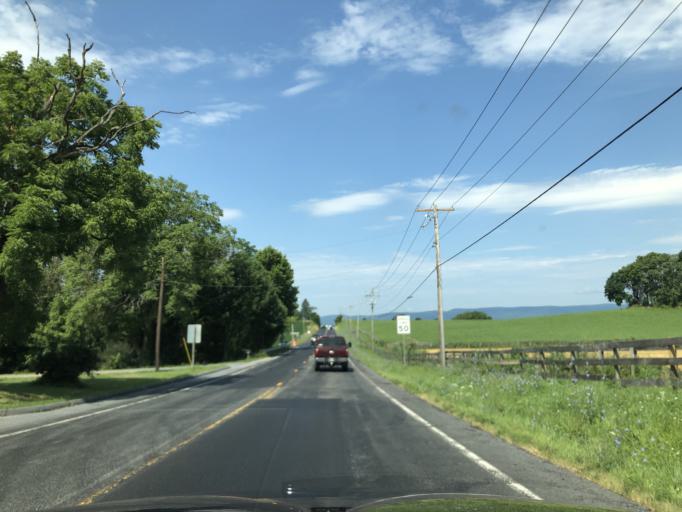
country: US
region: Maryland
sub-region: Frederick County
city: Walkersville
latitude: 39.4533
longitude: -77.3351
